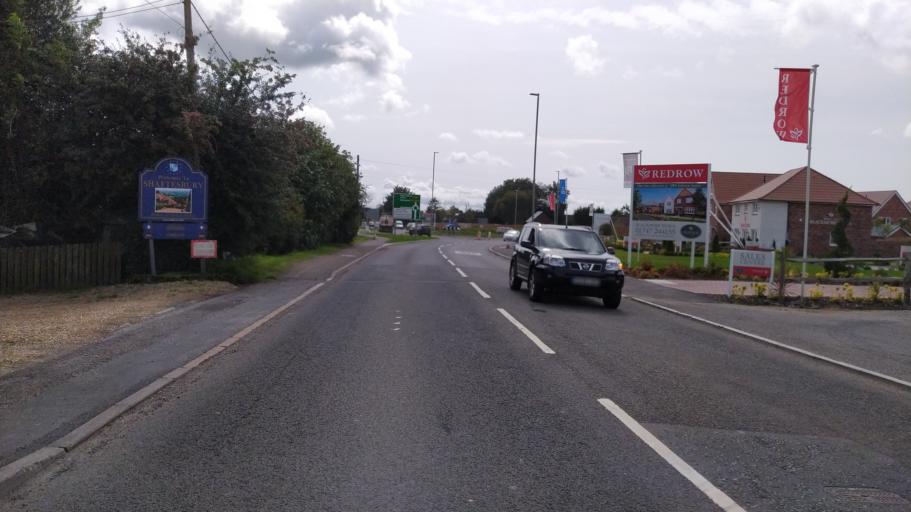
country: GB
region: England
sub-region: Dorset
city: Shaftesbury
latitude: 51.0165
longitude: -2.1892
